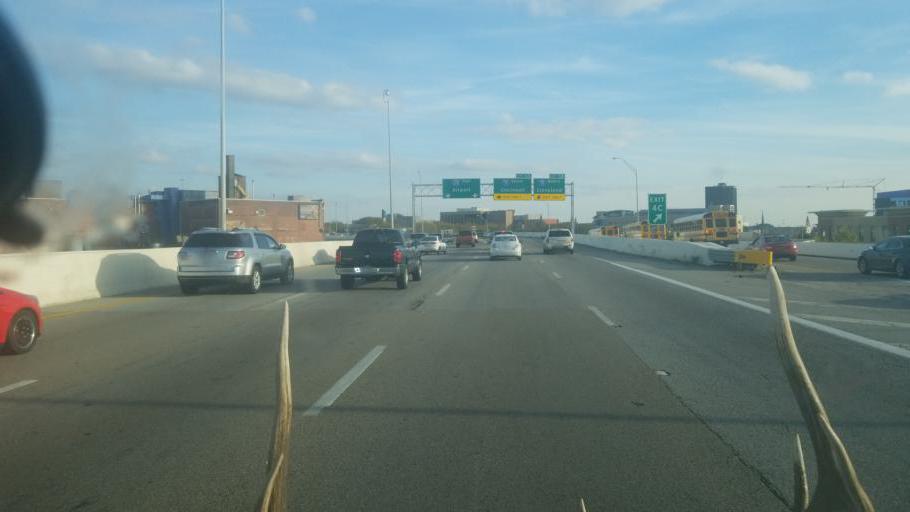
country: US
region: Ohio
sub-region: Franklin County
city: Columbus
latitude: 39.9735
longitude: -82.9931
